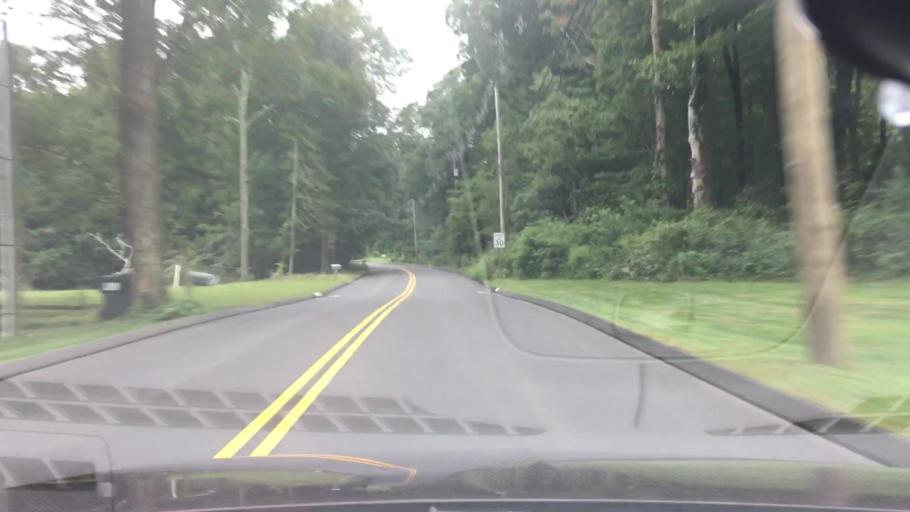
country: US
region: Connecticut
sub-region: New Haven County
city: Madison
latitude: 41.3087
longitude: -72.5992
